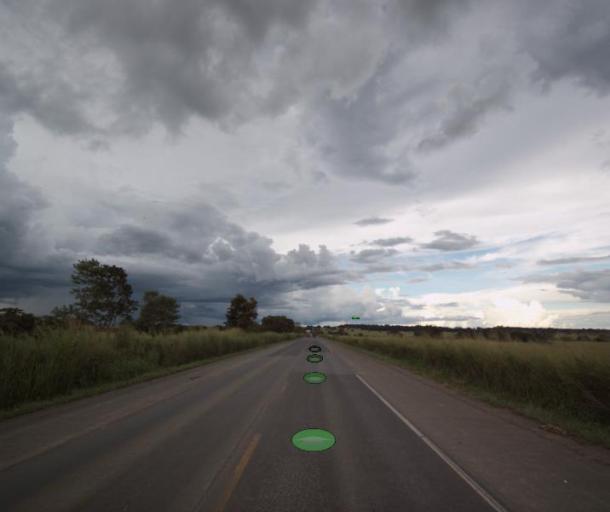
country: BR
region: Goias
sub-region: Itapaci
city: Itapaci
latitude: -15.0571
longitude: -49.4490
